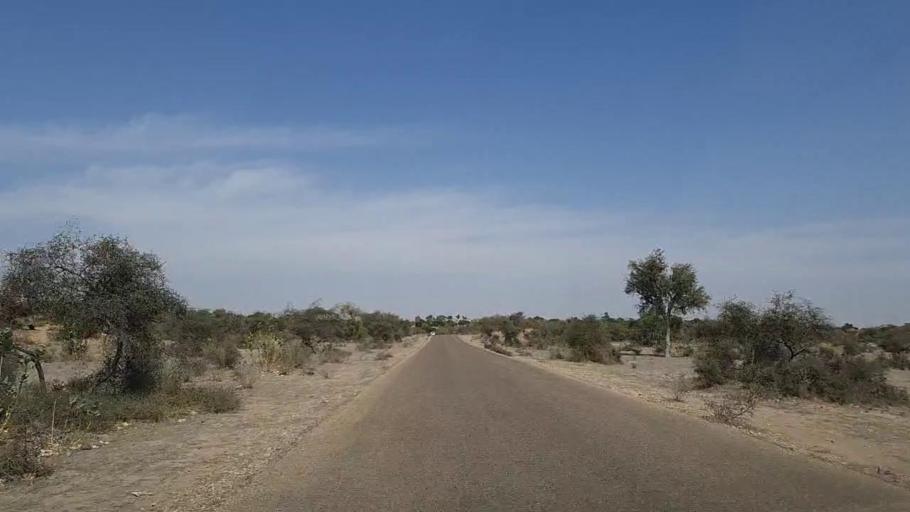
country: PK
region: Sindh
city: Nabisar
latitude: 25.0939
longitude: 69.9917
